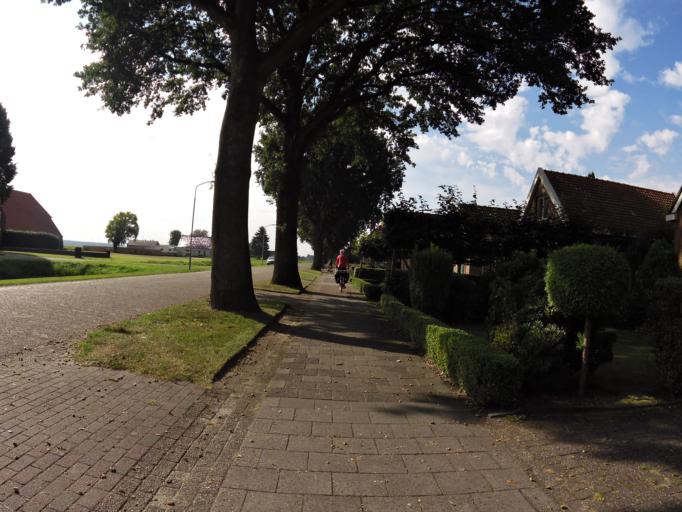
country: NL
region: Drenthe
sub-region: Gemeente Emmen
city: Klazienaveen
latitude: 52.7182
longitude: 7.0467
